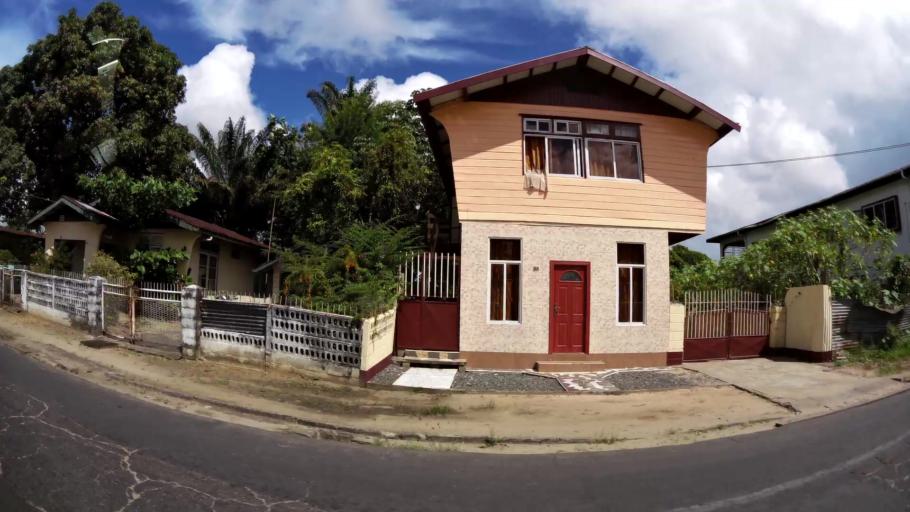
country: SR
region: Paramaribo
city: Paramaribo
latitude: 5.8303
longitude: -55.1742
